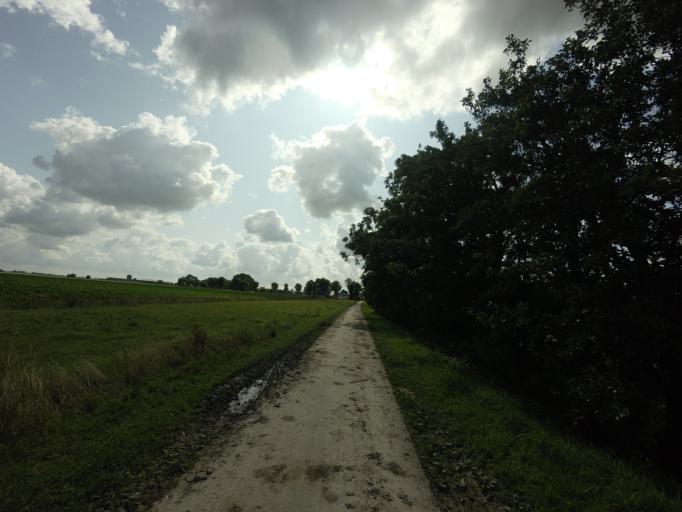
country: NL
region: Friesland
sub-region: Gemeente Het Bildt
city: Minnertsga
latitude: 53.2595
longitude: 5.5961
